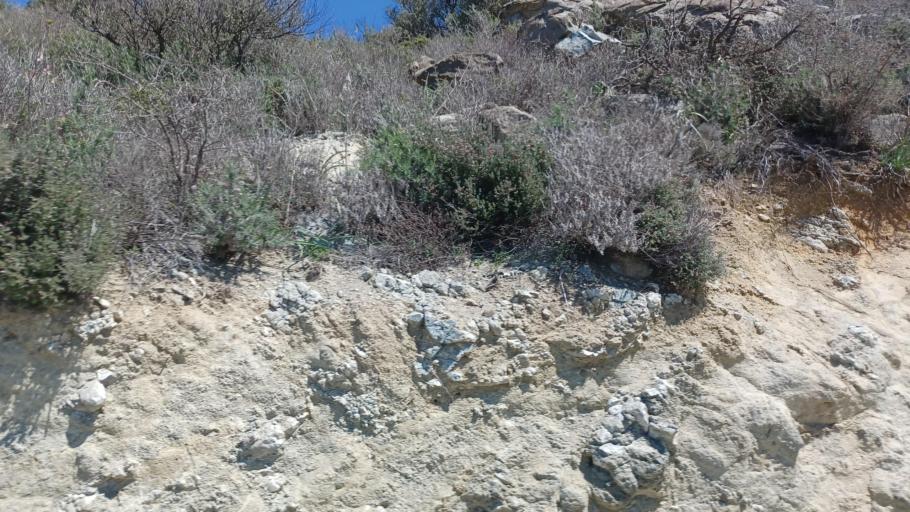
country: CY
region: Limassol
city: Parekklisha
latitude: 34.8056
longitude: 33.1741
